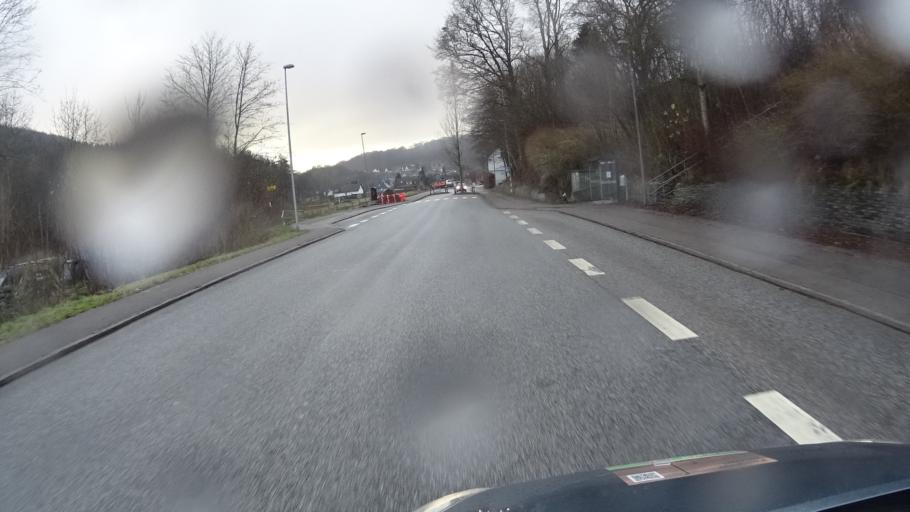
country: DK
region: South Denmark
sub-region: Vejle Kommune
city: Vejle
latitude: 55.7407
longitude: 9.5350
